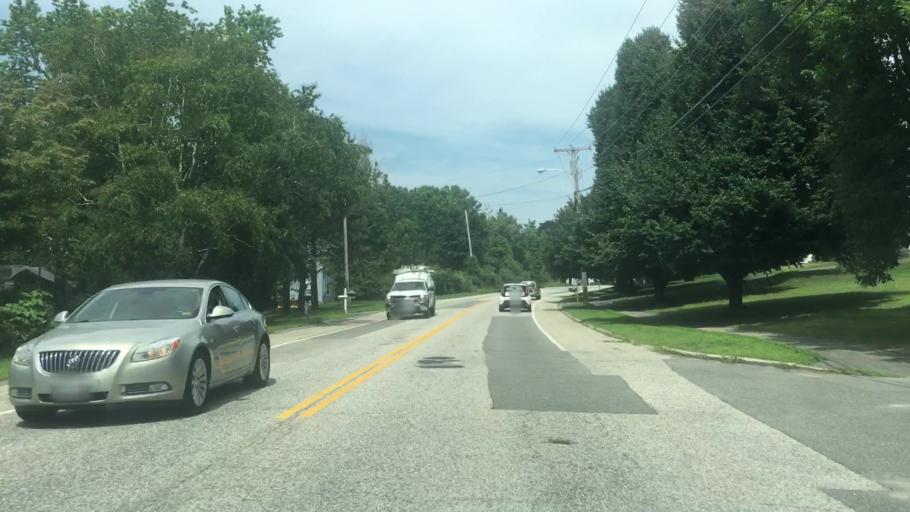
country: US
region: Maine
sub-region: Cumberland County
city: South Portland Gardens
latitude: 43.6116
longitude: -70.2800
